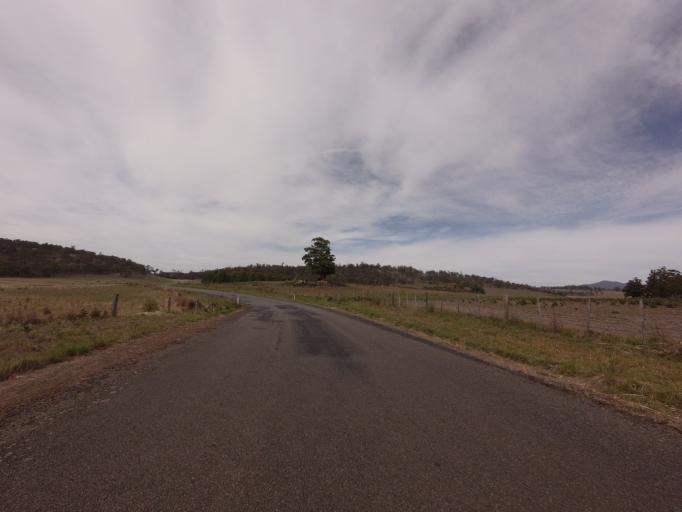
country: AU
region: Tasmania
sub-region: Sorell
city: Sorell
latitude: -42.5260
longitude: 147.6509
